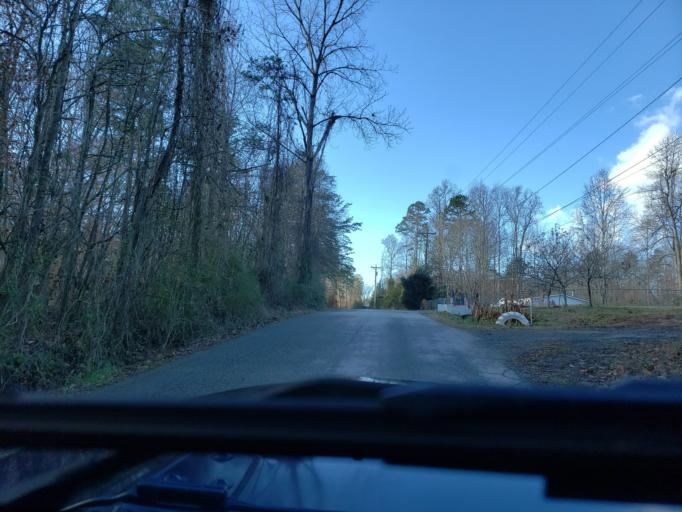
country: US
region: North Carolina
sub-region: Cleveland County
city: Kings Mountain
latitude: 35.1584
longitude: -81.3387
